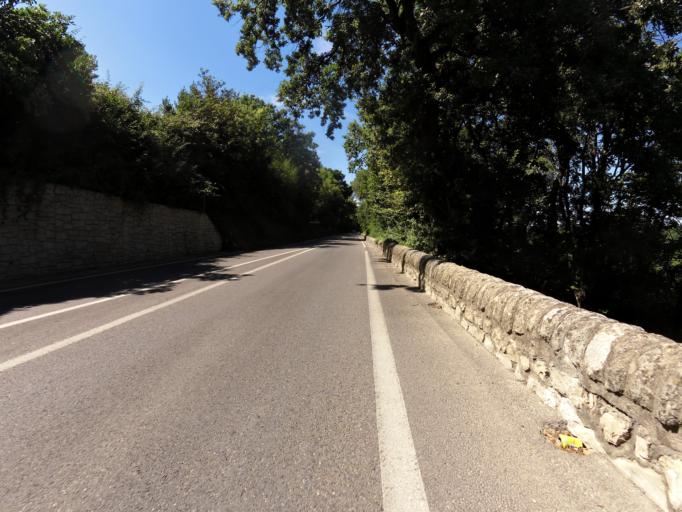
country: FR
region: Languedoc-Roussillon
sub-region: Departement du Gard
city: Sommieres
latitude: 43.7901
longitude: 4.0811
